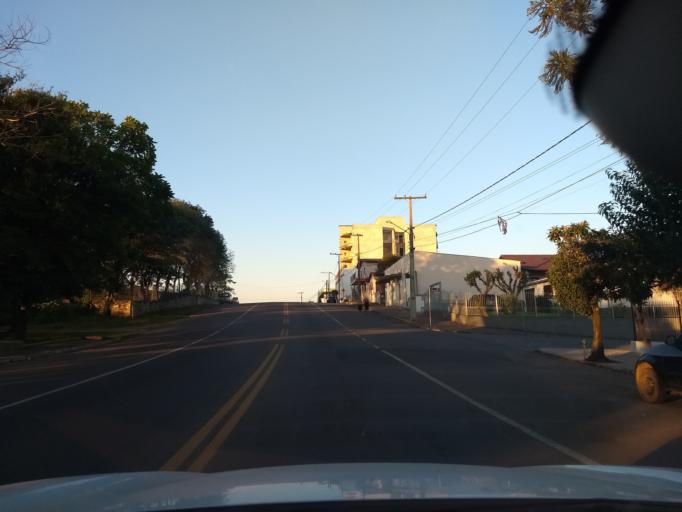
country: BR
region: Rio Grande do Sul
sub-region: Santa Cruz Do Sul
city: Santa Cruz do Sul
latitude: -29.7189
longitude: -52.5119
